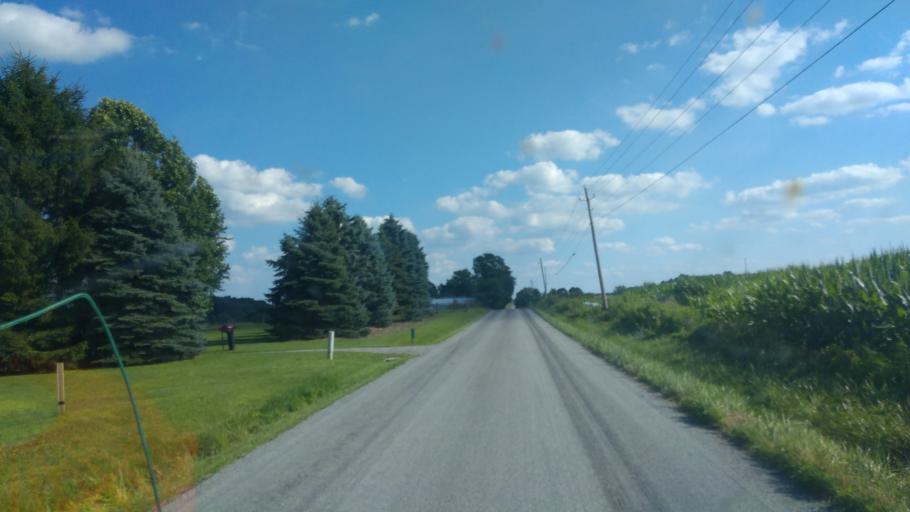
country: US
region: Ohio
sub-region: Wayne County
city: Apple Creek
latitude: 40.7136
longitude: -81.9059
